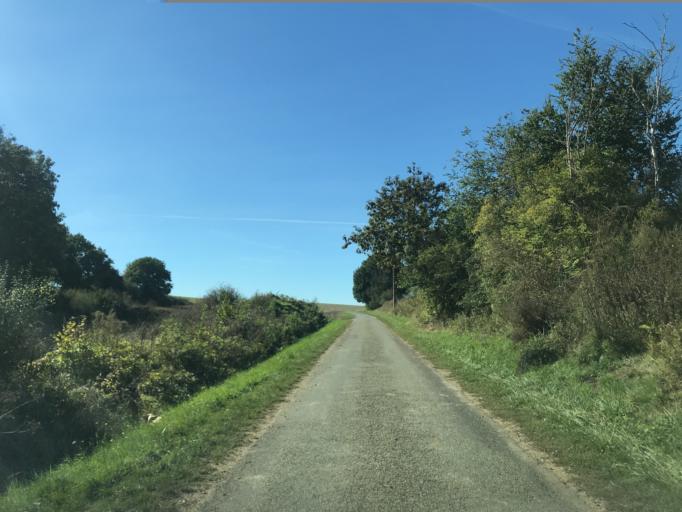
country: FR
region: Haute-Normandie
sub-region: Departement de l'Eure
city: Ande
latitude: 49.1742
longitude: 1.2691
